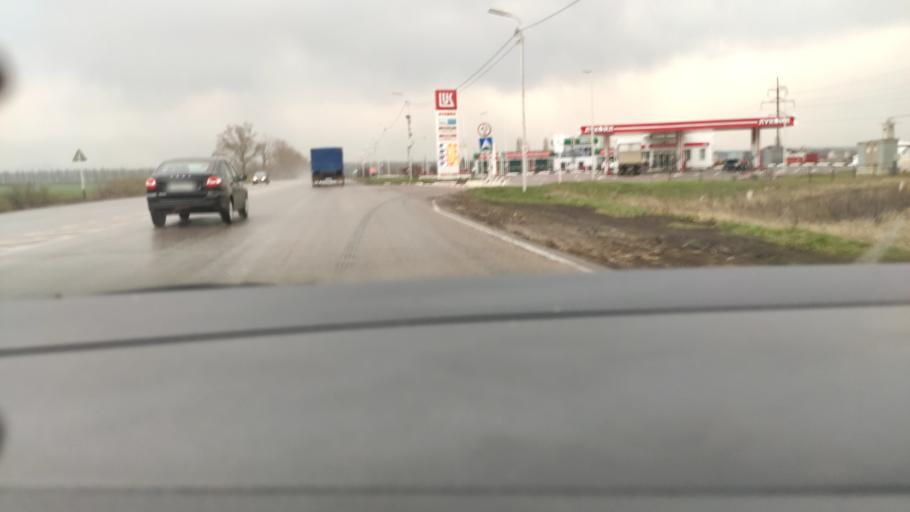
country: RU
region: Voronezj
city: Maslovka
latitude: 51.5079
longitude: 39.3057
